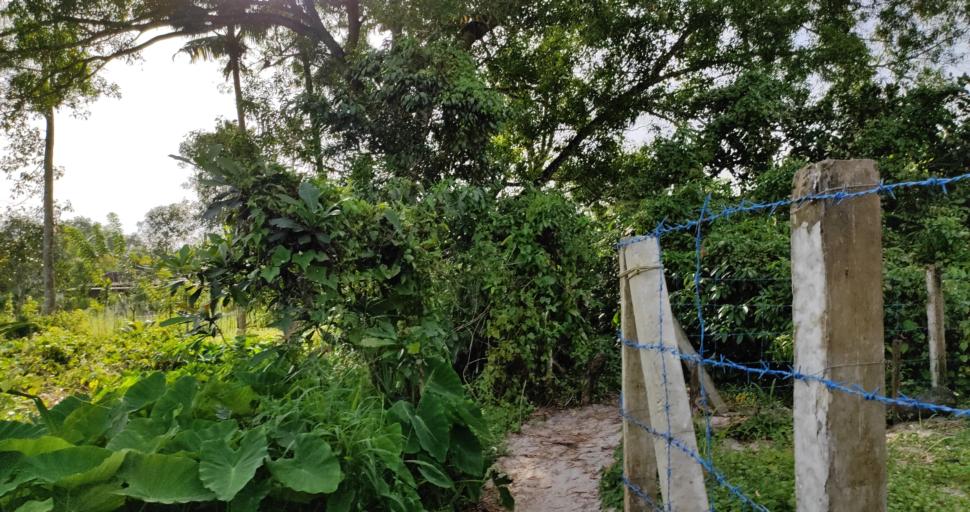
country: IN
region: Kerala
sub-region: Alappuzha
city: Shertallai
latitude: 9.6333
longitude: 76.3362
